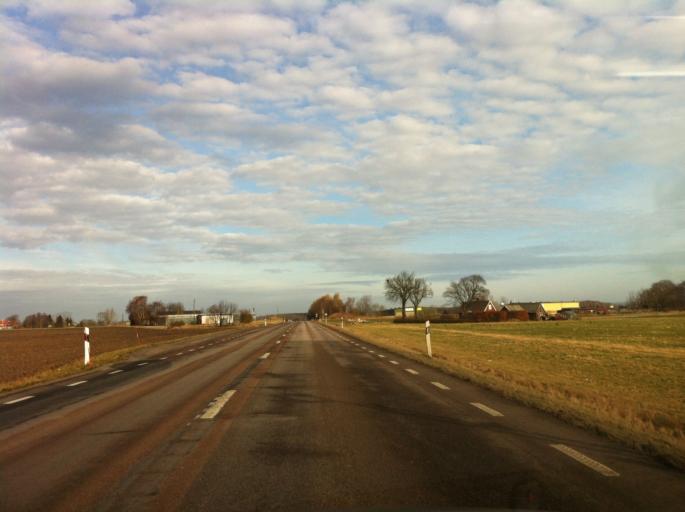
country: SE
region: Skane
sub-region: Bjuvs Kommun
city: Billesholm
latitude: 56.0002
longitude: 12.9491
